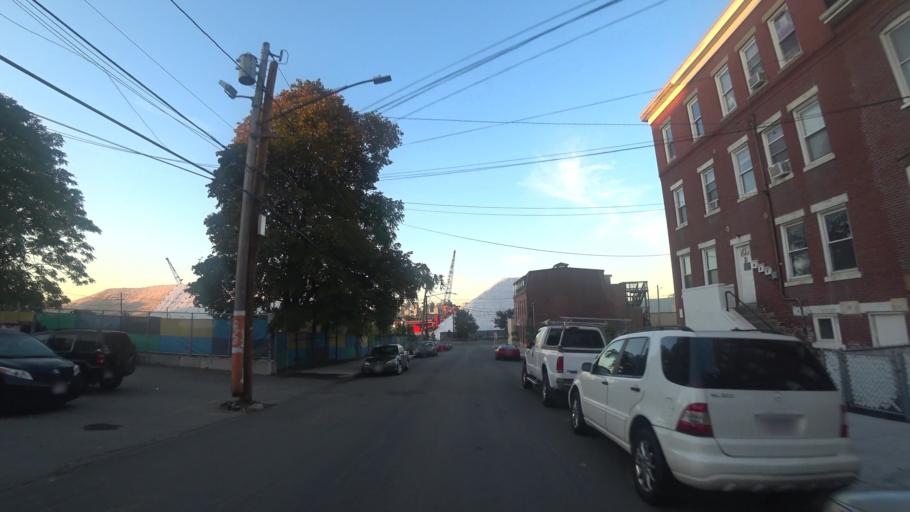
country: US
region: Massachusetts
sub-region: Suffolk County
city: Chelsea
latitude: 42.3887
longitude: -71.0368
